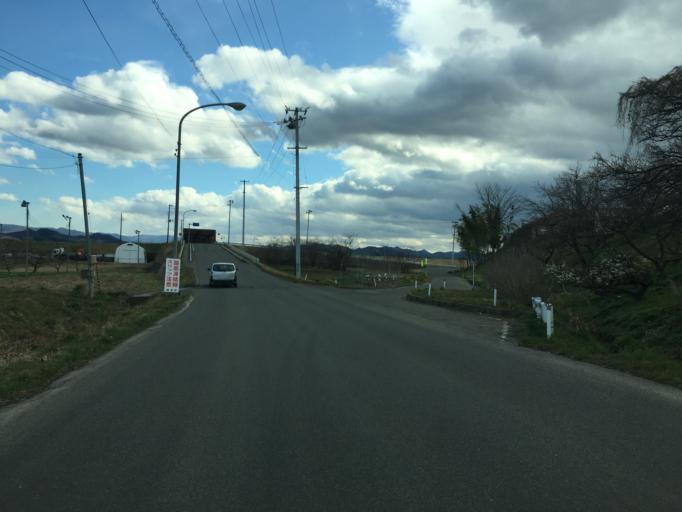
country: JP
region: Fukushima
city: Yanagawamachi-saiwaicho
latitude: 37.8653
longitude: 140.5682
